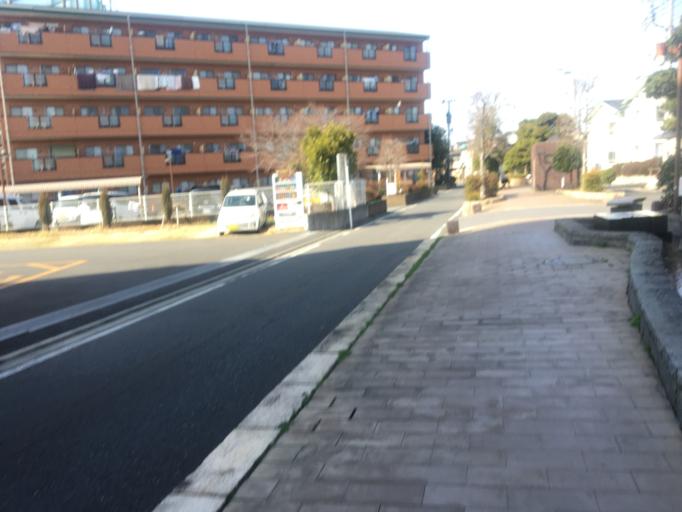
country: JP
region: Saitama
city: Shiki
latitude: 35.8434
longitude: 139.5869
